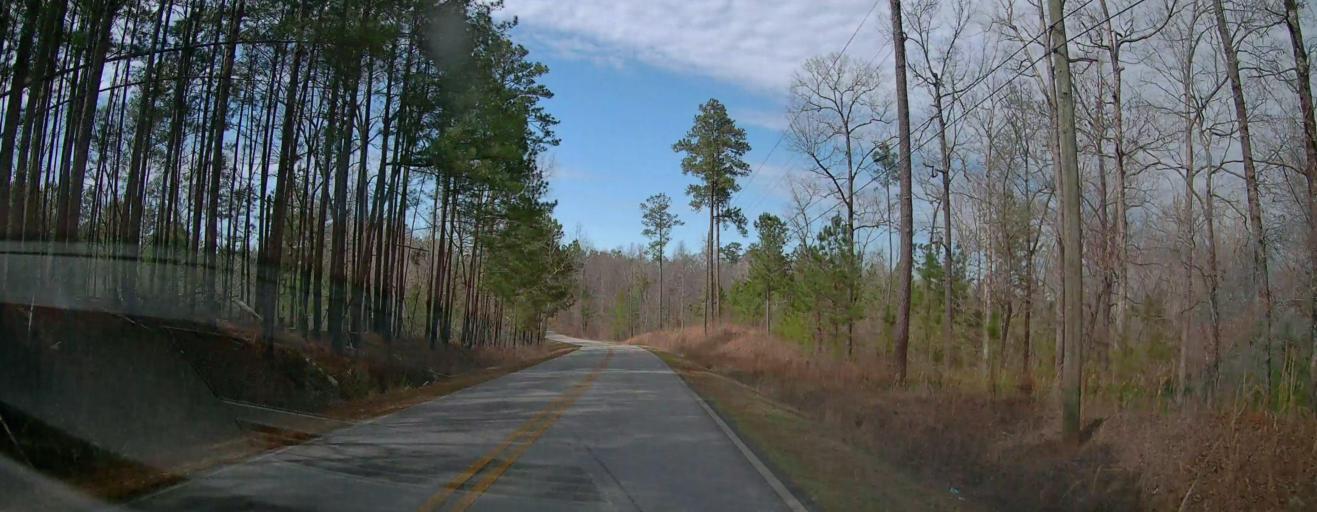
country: US
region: Georgia
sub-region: Jones County
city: Gray
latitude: 33.0291
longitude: -83.7038
